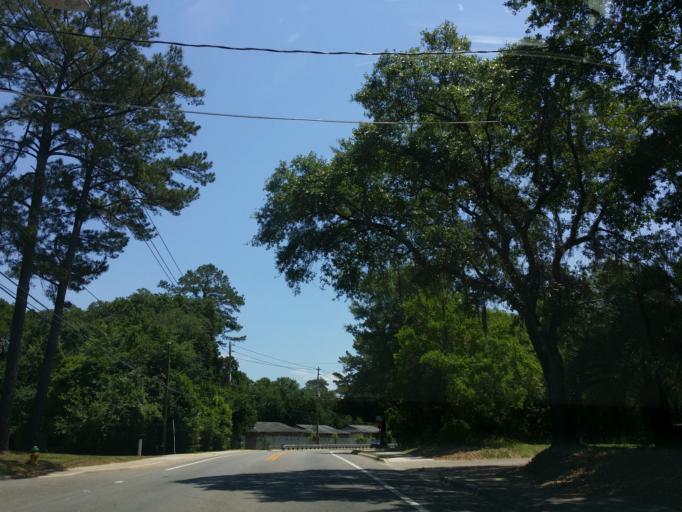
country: US
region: Florida
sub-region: Leon County
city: Tallahassee
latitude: 30.4731
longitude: -84.3162
